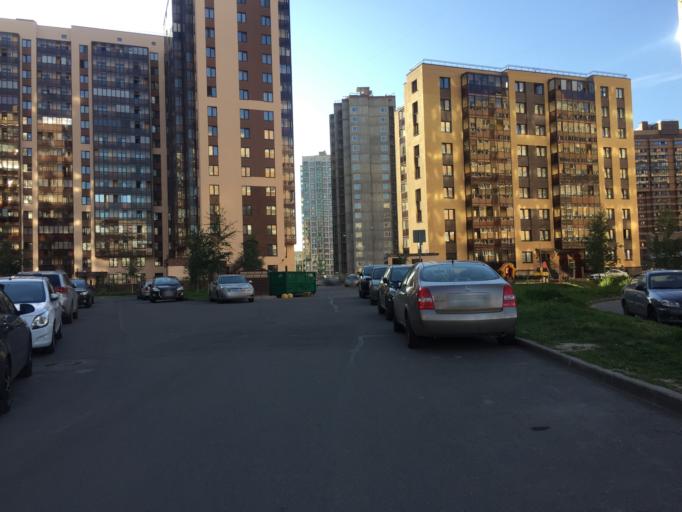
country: RU
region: Leningrad
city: Murino
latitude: 60.0544
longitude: 30.4321
